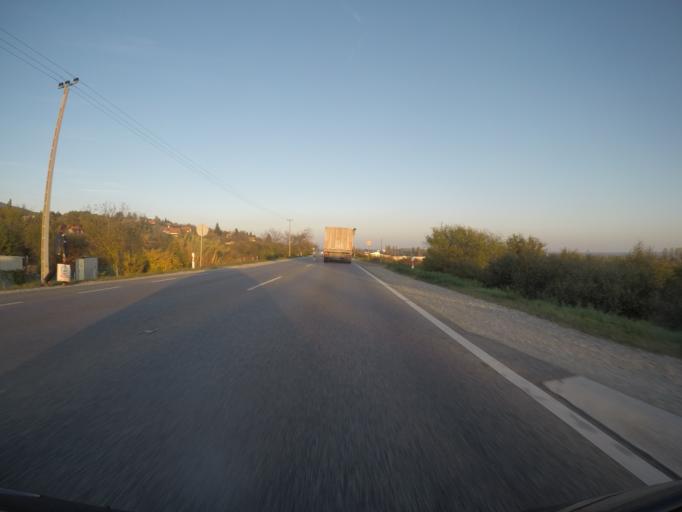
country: HU
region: Baranya
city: Pellerd
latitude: 46.0616
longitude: 18.1380
